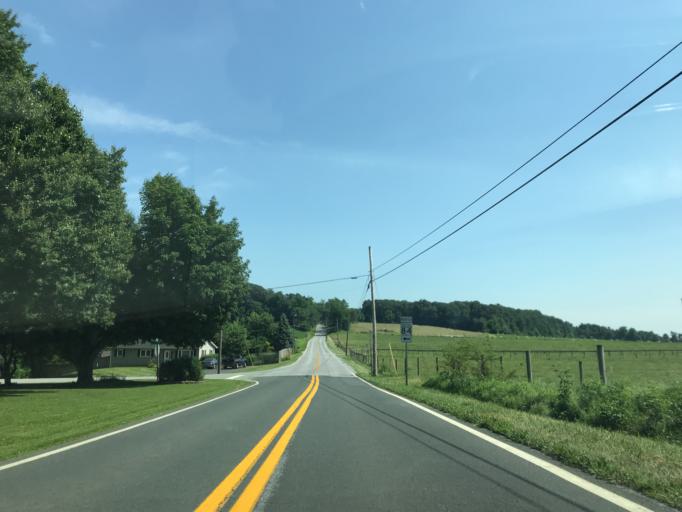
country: US
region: Maryland
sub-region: Carroll County
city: New Windsor
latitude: 39.6022
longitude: -77.1227
